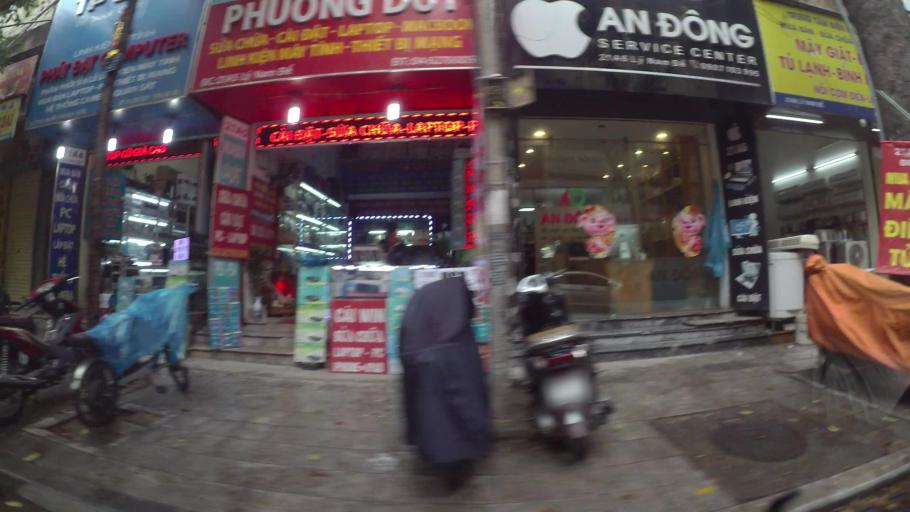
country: VN
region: Ha Noi
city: Hoan Kiem
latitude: 21.0372
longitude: 105.8453
